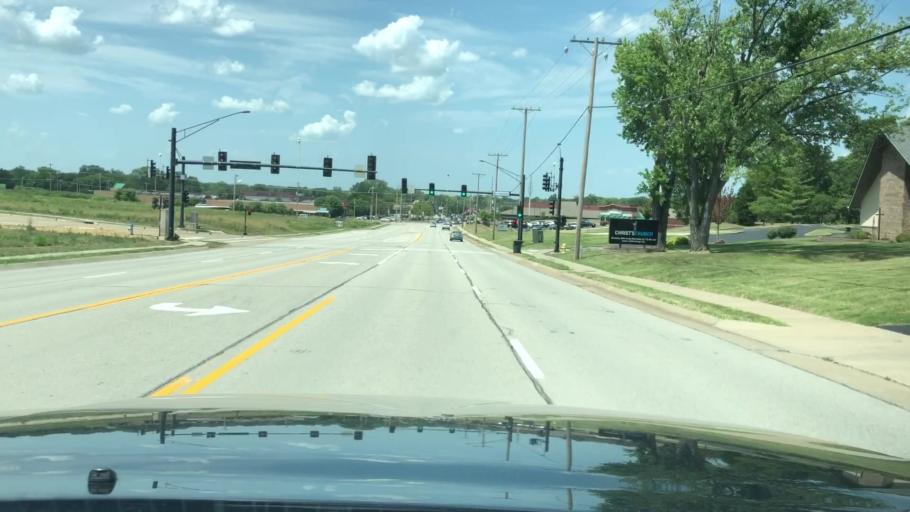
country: US
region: Missouri
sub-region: Saint Charles County
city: Saint Peters
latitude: 38.7882
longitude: -90.6209
